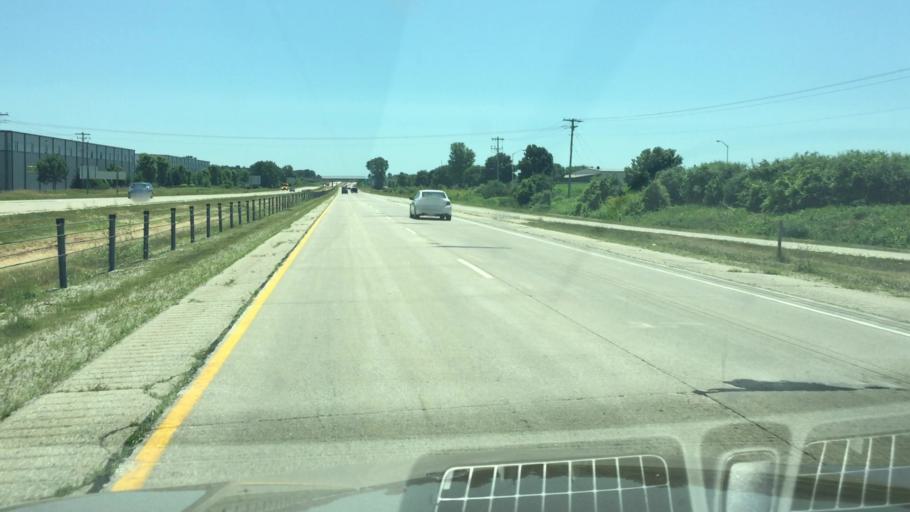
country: US
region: Wisconsin
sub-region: Dodge County
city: Beaver Dam
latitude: 43.4743
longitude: -88.8154
